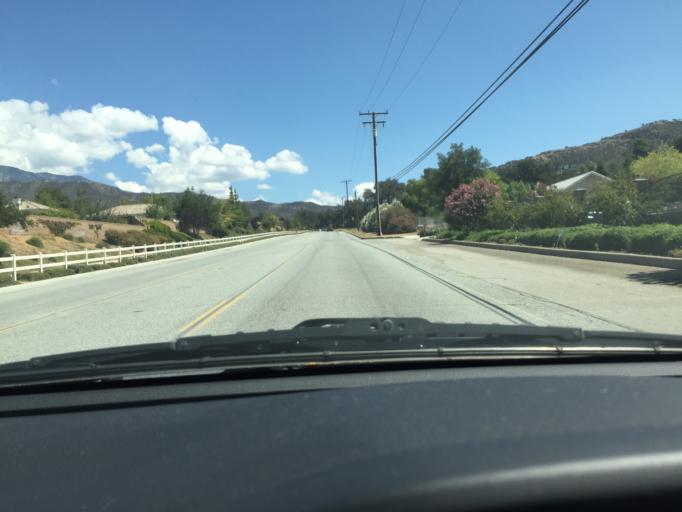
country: US
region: California
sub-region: San Bernardino County
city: Yucaipa
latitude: 34.0152
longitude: -117.0133
